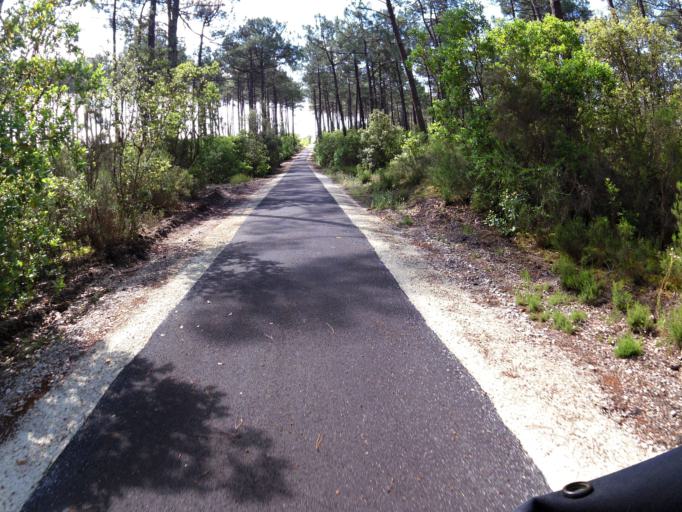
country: FR
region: Aquitaine
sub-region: Departement de la Gironde
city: Lacanau
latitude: 45.0349
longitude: -1.1816
